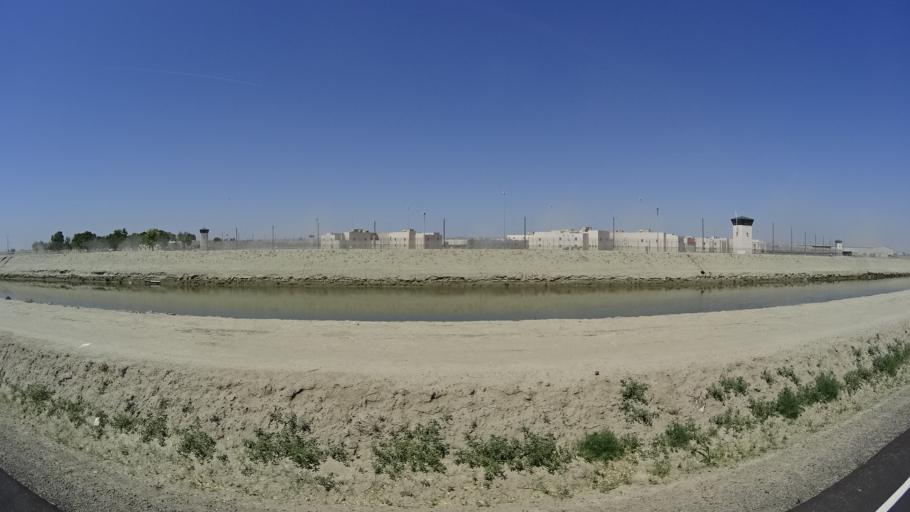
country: US
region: California
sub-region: Kings County
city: Corcoran
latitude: 36.0538
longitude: -119.5362
